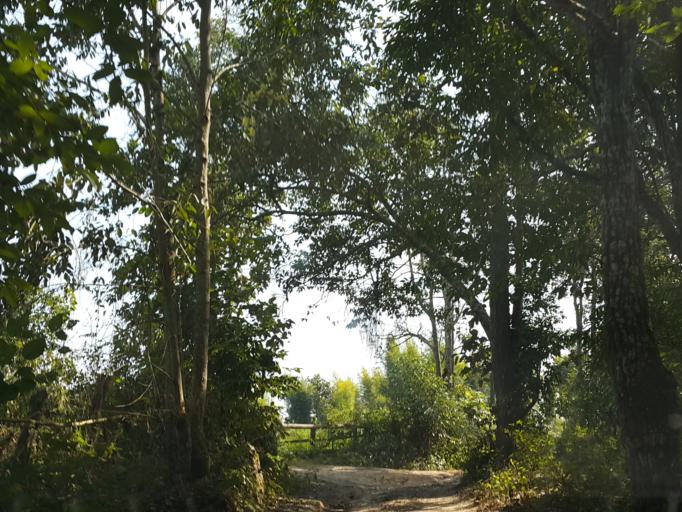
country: TH
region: Chiang Mai
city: Hot
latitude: 18.1224
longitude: 98.4405
